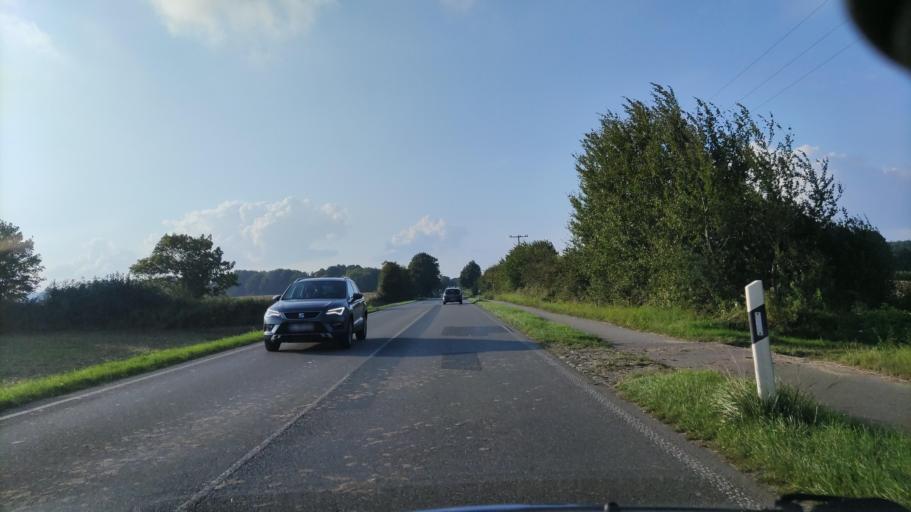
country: DE
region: Schleswig-Holstein
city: Ahrensbok
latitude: 53.9601
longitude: 10.6107
